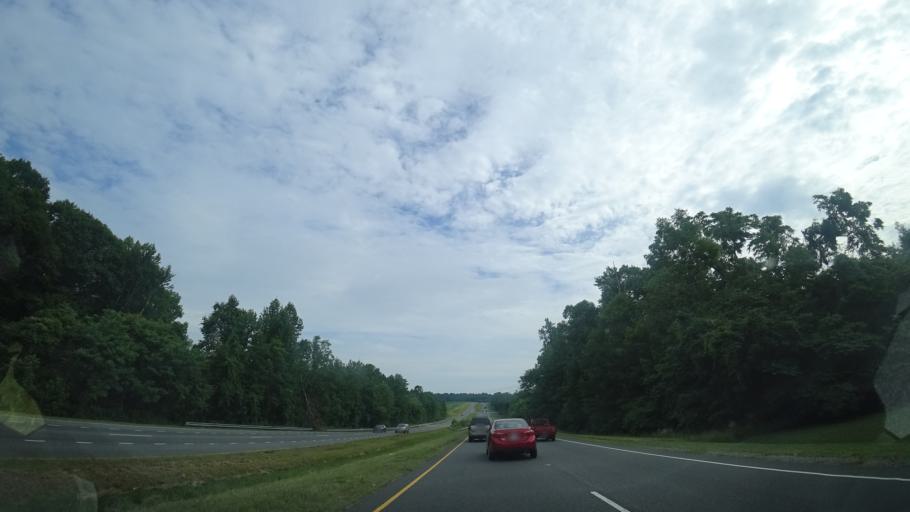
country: US
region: Virginia
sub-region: Spotsylvania County
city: Spotsylvania
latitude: 38.2160
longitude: -77.5706
